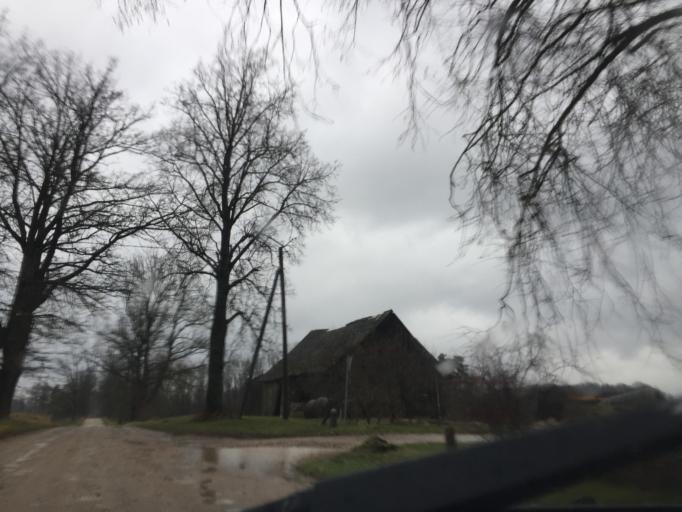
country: LV
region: Limbazu Rajons
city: Limbazi
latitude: 57.6544
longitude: 24.7764
